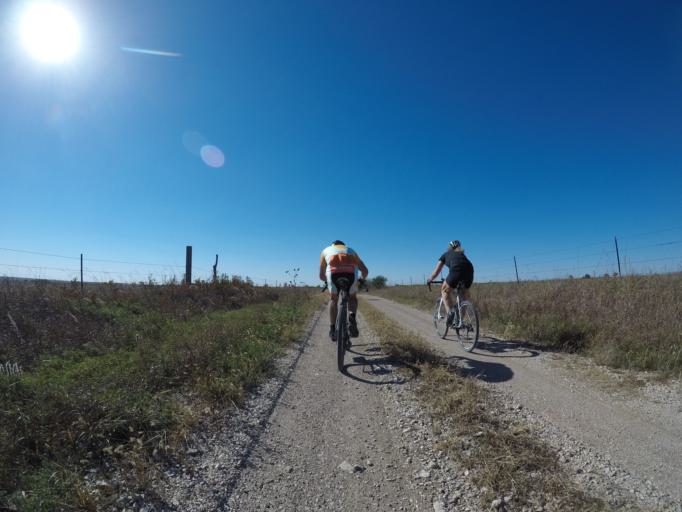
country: US
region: Kansas
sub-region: Wabaunsee County
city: Alma
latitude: 38.9711
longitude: -96.4595
